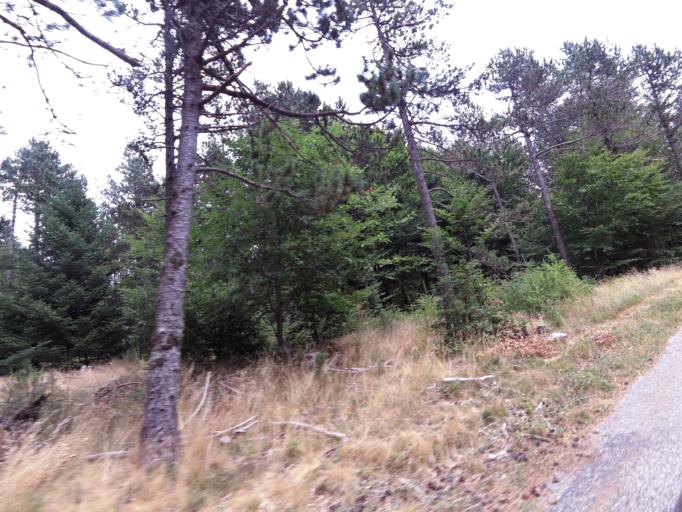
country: FR
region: Languedoc-Roussillon
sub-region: Departement du Gard
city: Valleraugue
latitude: 44.0648
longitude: 3.6043
